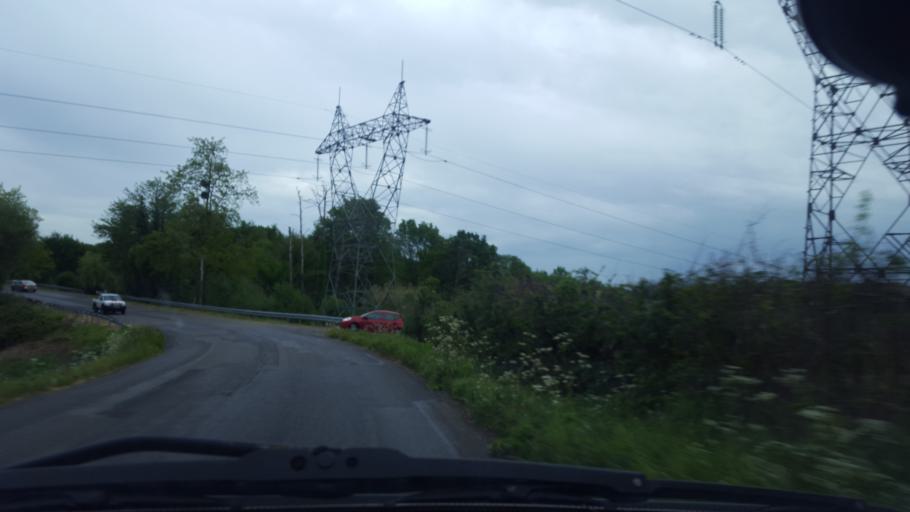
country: FR
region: Pays de la Loire
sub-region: Departement de la Loire-Atlantique
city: Les Sorinieres
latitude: 47.1643
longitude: -1.5208
